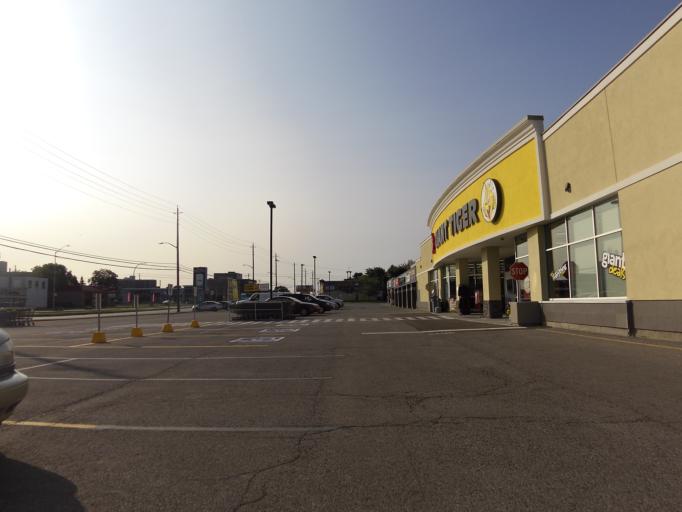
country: CA
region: Ontario
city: Ottawa
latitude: 45.3572
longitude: -75.7378
